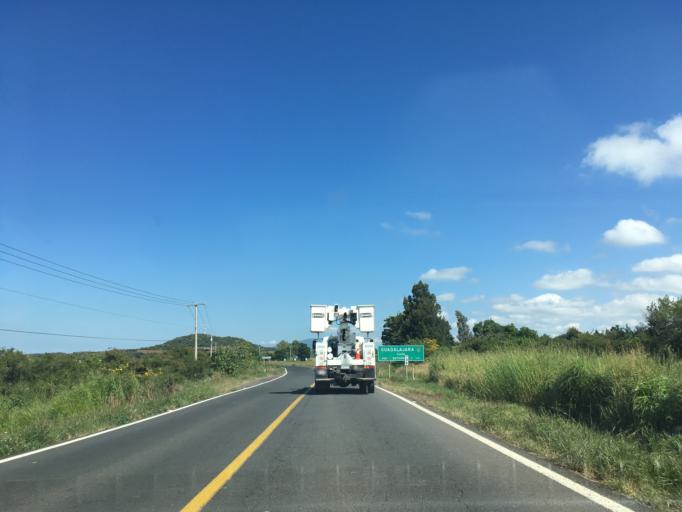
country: MX
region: Michoacan
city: Churintzio
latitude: 20.1262
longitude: -102.0681
